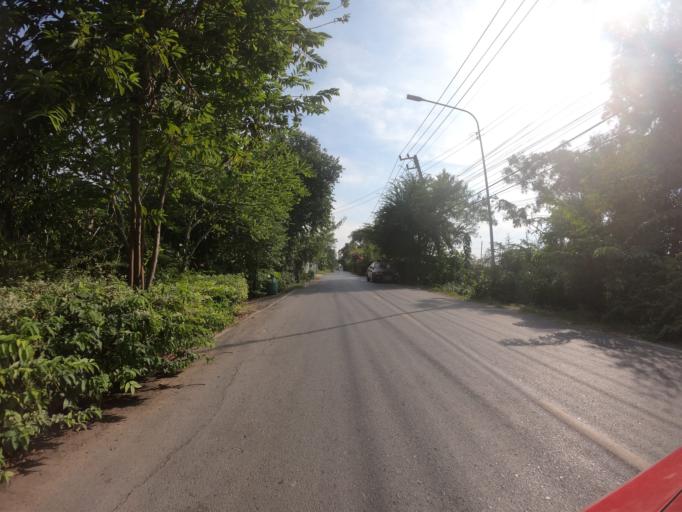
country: TH
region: Pathum Thani
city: Thanyaburi
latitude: 14.0113
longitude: 100.7320
